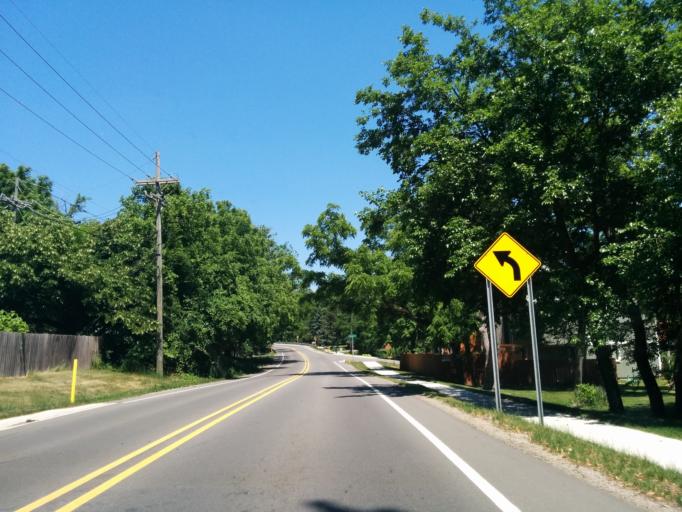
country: US
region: Michigan
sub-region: Oakland County
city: West Bloomfield Township
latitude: 42.5767
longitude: -83.4137
